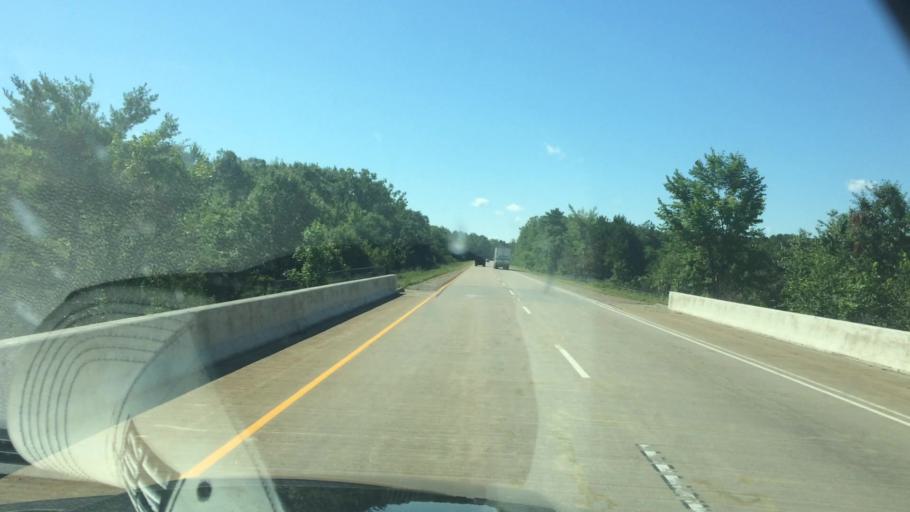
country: US
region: Wisconsin
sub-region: Marathon County
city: Mosinee
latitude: 44.6946
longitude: -89.6459
